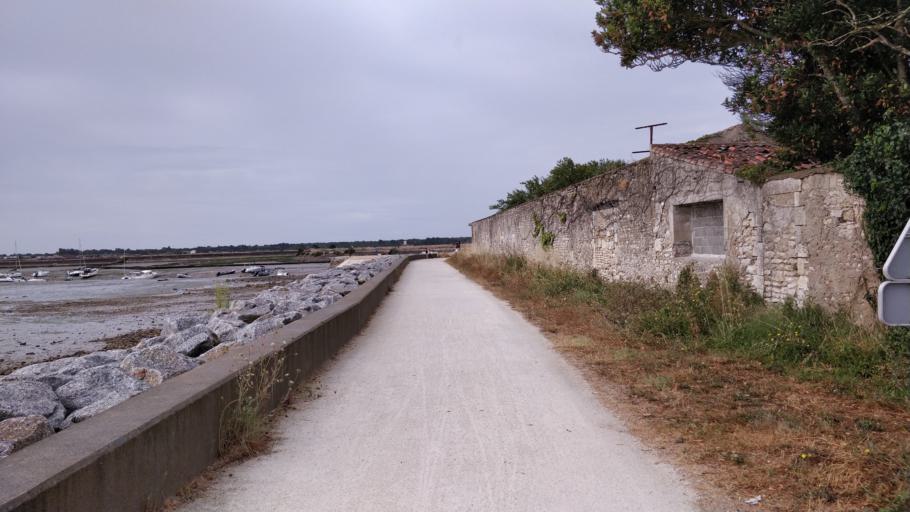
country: FR
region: Poitou-Charentes
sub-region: Departement de la Charente-Maritime
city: La Couarde-sur-Mer
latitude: 46.2171
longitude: -1.4379
